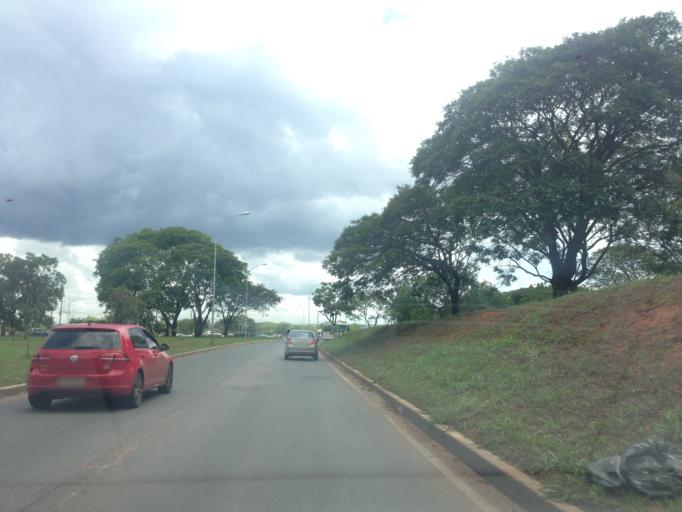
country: BR
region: Federal District
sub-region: Brasilia
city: Brasilia
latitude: -15.8099
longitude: -47.9401
